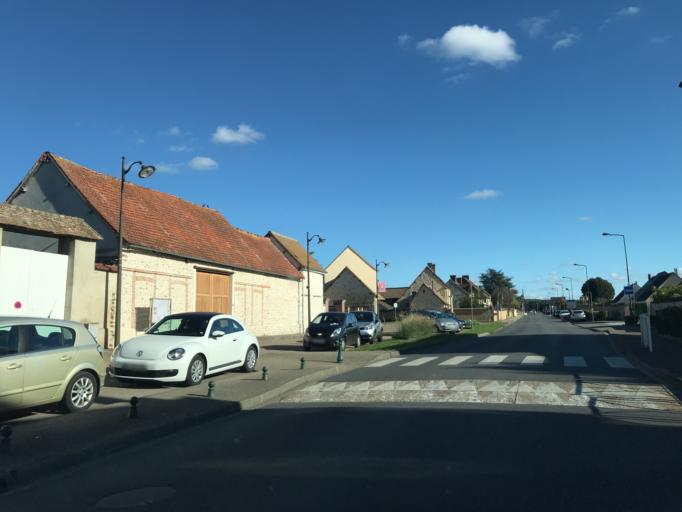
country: FR
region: Haute-Normandie
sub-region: Departement de l'Eure
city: Saint-Aubin-sur-Gaillon
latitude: 49.0962
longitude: 1.2792
